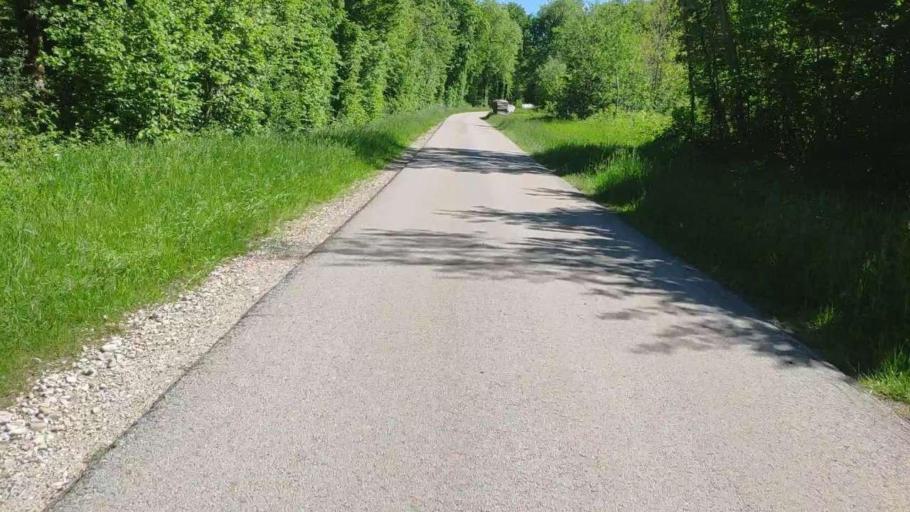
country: FR
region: Franche-Comte
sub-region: Departement du Jura
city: Poligny
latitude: 46.7468
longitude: 5.7743
